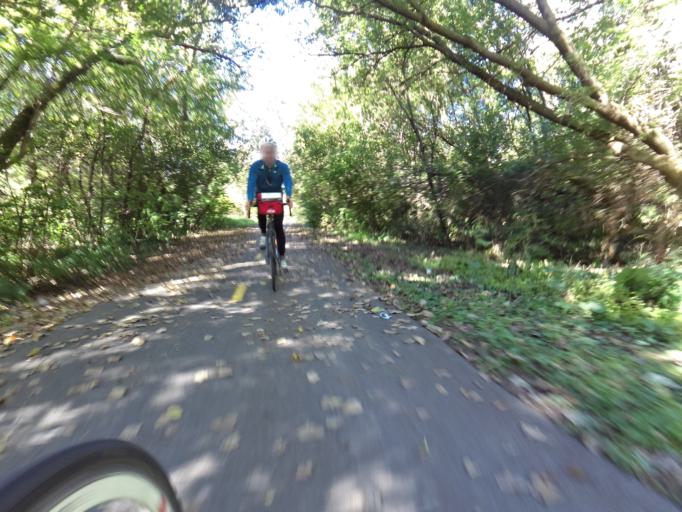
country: CA
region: Quebec
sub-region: Outaouais
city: Gatineau
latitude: 45.4770
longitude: -75.6469
